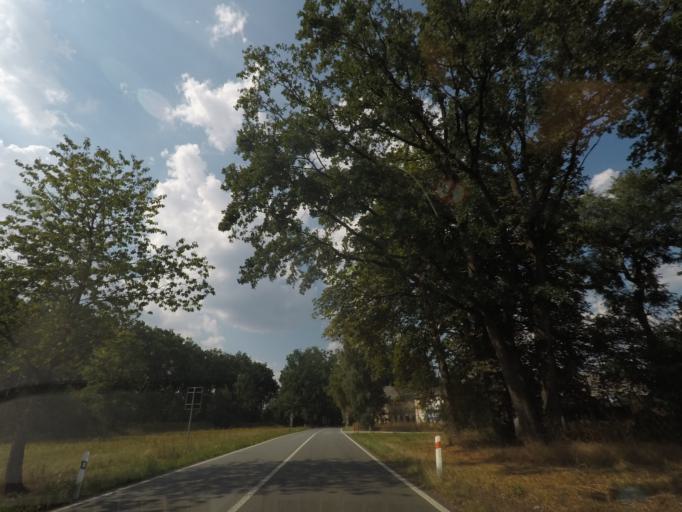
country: CZ
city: Albrechtice nad Orlici
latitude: 50.1275
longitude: 16.0650
